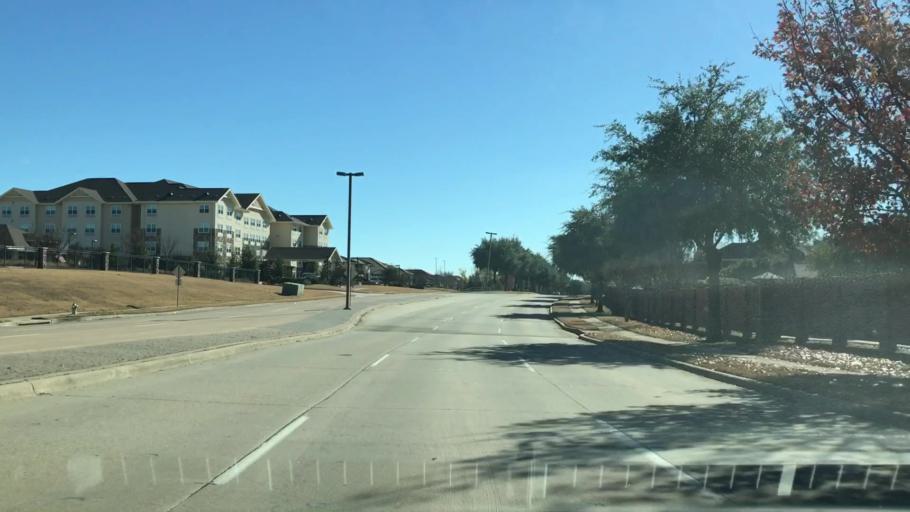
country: US
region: Texas
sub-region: Dallas County
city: Coppell
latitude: 32.9129
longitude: -96.9650
